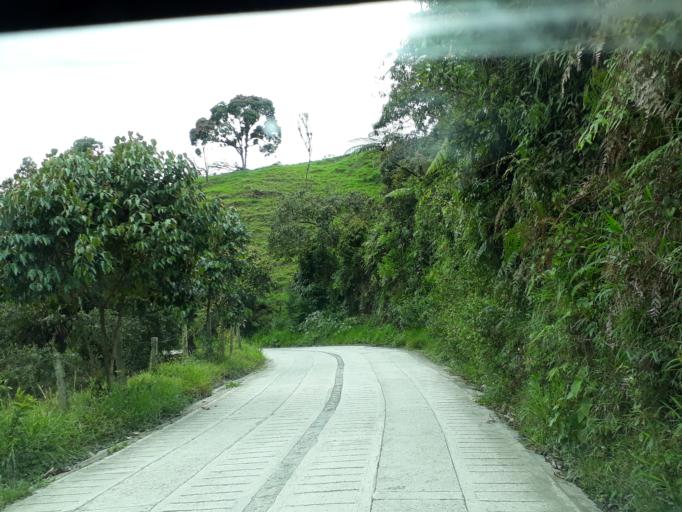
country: CO
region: Cundinamarca
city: Topaipi
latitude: 5.2646
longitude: -74.1914
